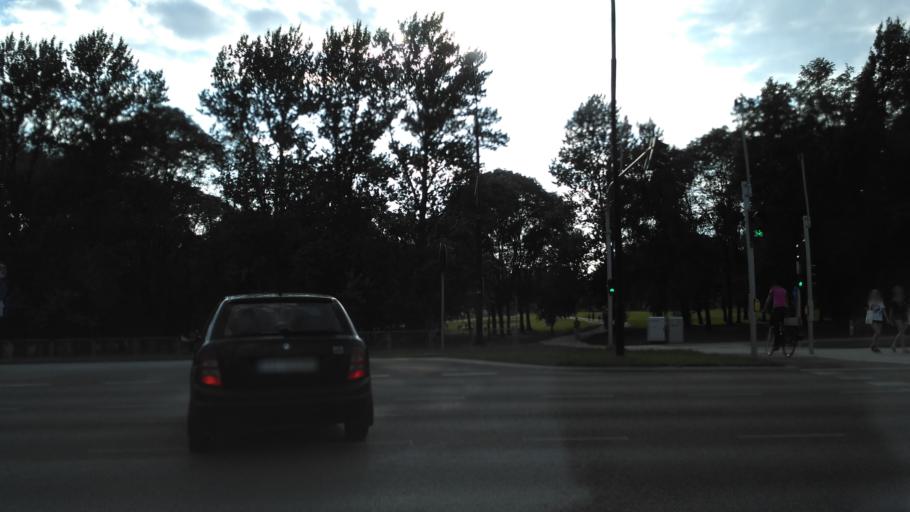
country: PL
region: Lublin Voivodeship
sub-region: Powiat lubelski
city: Lublin
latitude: 51.2492
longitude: 22.5748
